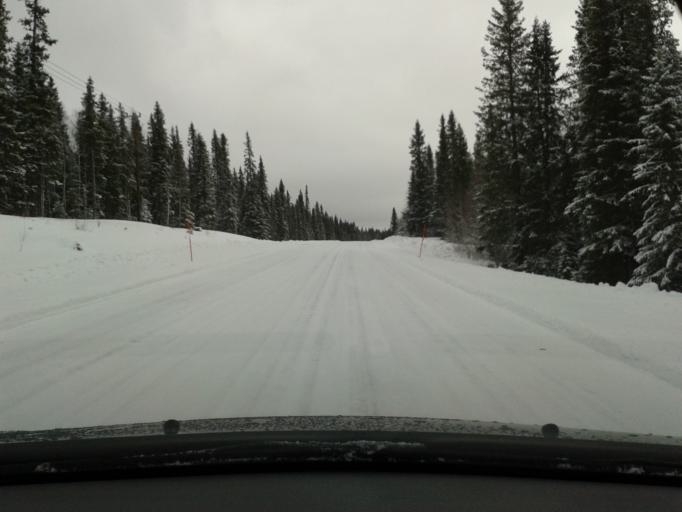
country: SE
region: Vaesterbotten
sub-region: Vilhelmina Kommun
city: Sjoberg
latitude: 65.2373
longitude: 15.8229
